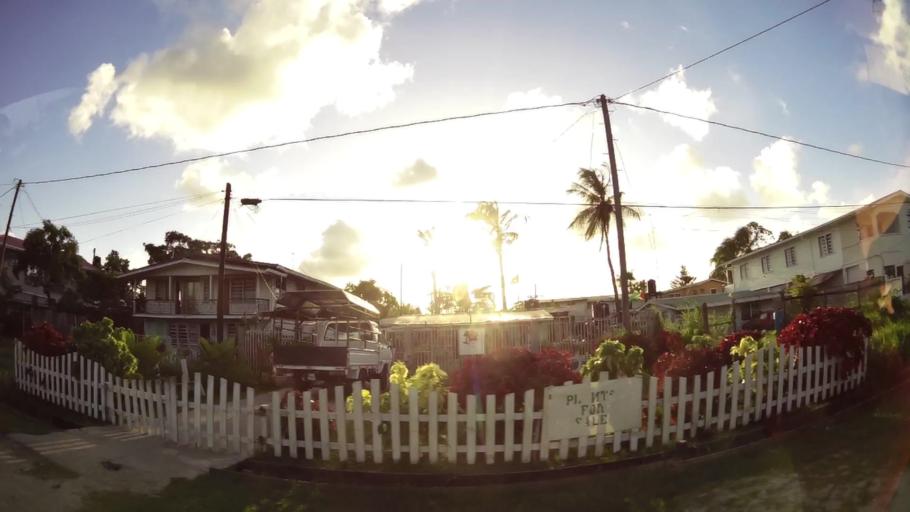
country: GY
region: Demerara-Mahaica
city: Georgetown
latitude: 6.7912
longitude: -58.1539
